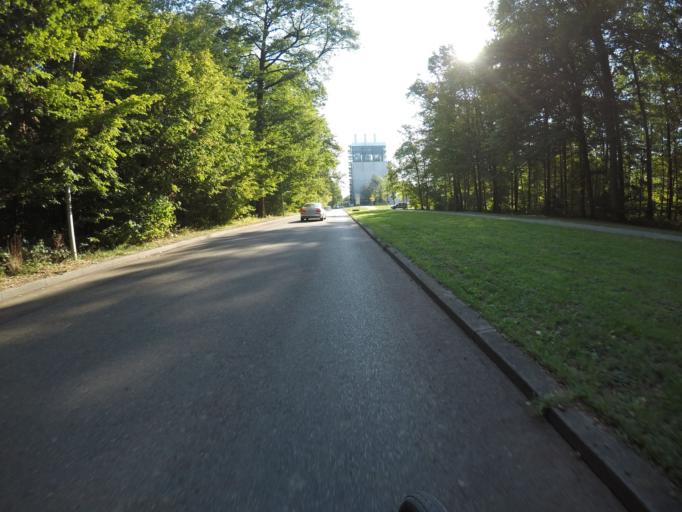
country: DE
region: Baden-Wuerttemberg
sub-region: Regierungsbezirk Stuttgart
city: Gerlingen
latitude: 48.7510
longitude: 9.1071
